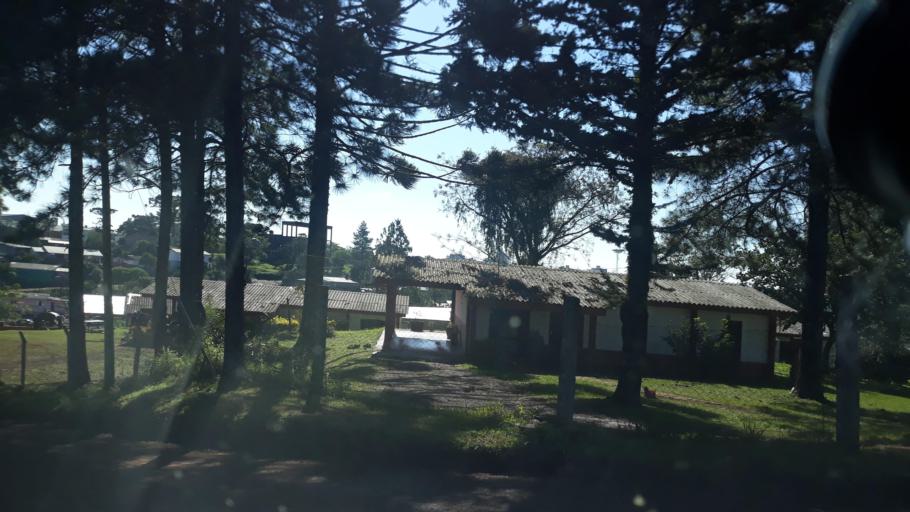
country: AR
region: Misiones
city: Bernardo de Irigoyen
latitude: -26.2615
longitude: -53.6466
